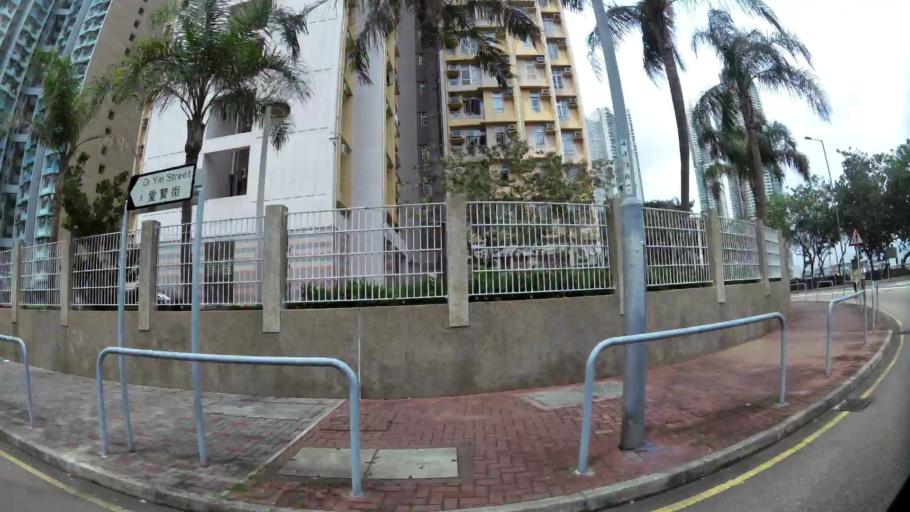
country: HK
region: Wanchai
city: Wan Chai
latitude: 22.2826
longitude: 114.2280
